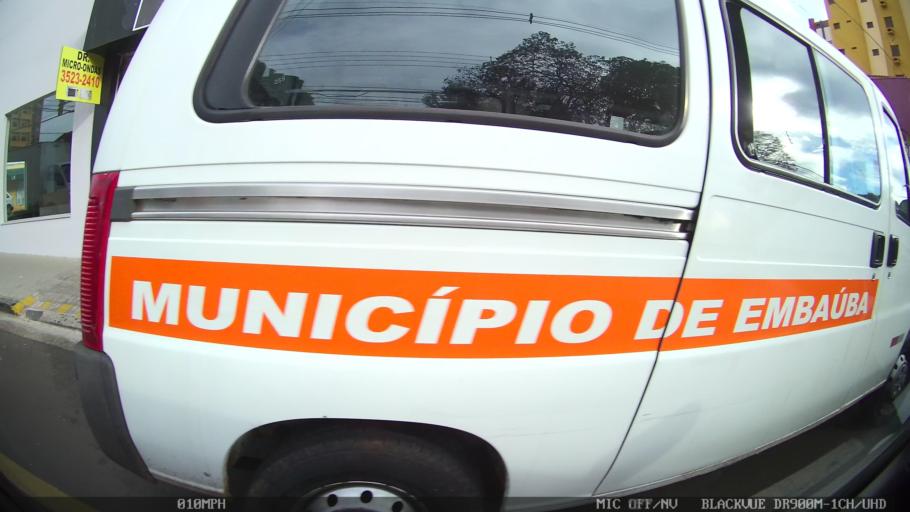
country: BR
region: Sao Paulo
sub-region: Catanduva
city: Catanduva
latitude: -21.1393
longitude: -48.9736
